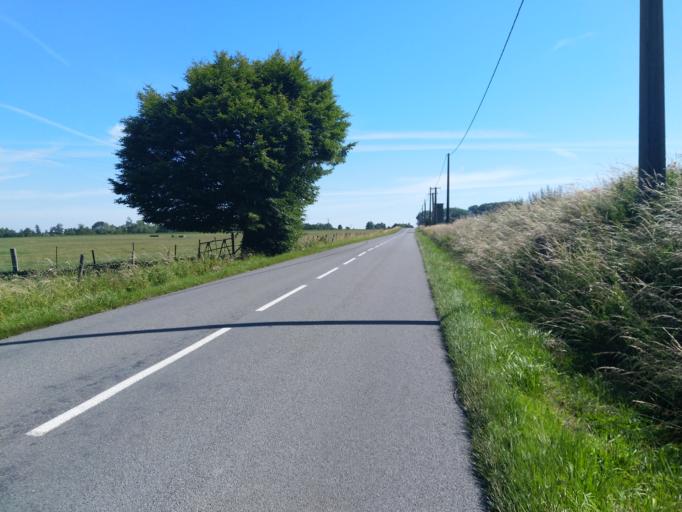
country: FR
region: Nord-Pas-de-Calais
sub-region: Departement du Nord
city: Bavay
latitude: 50.3085
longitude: 3.8043
